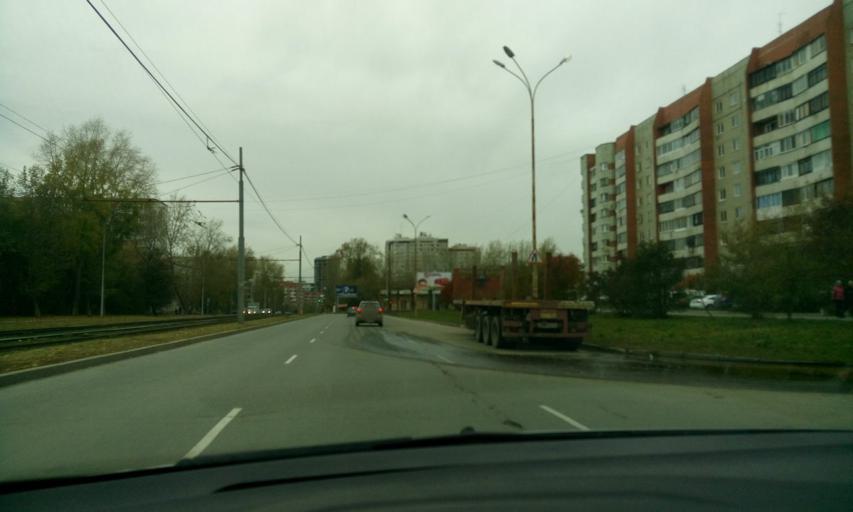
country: RU
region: Sverdlovsk
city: Yekaterinburg
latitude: 56.8587
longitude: 60.6296
